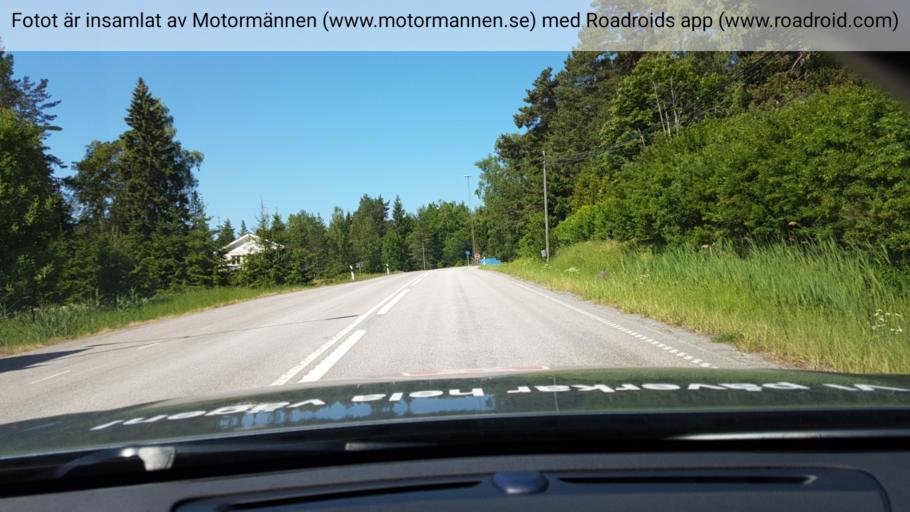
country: SE
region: Stockholm
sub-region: Norrtalje Kommun
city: Skanninge
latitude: 59.9052
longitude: 18.5831
